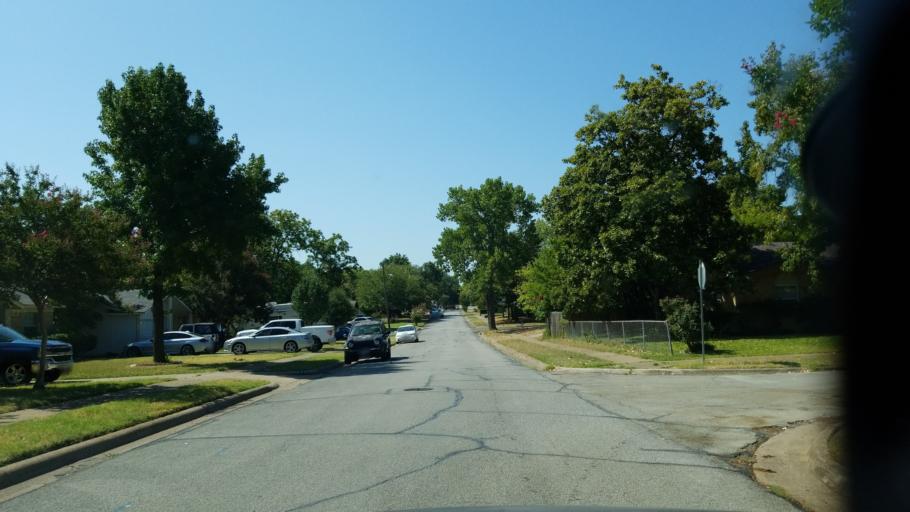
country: US
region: Texas
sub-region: Dallas County
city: Duncanville
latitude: 32.6431
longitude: -96.8990
